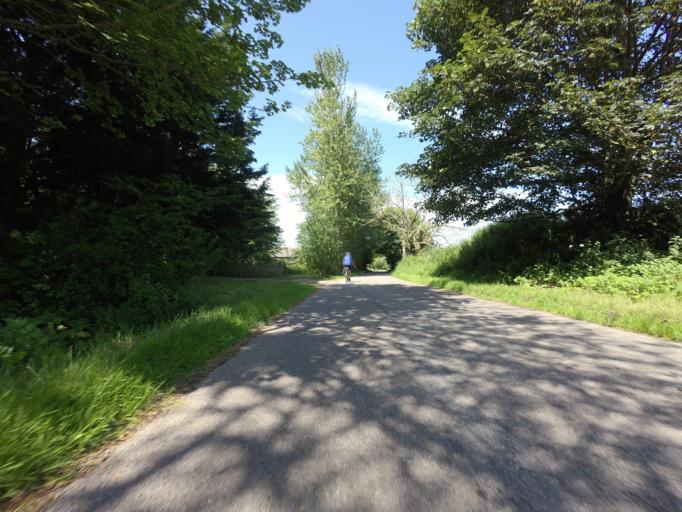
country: GB
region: Scotland
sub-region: Highland
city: Conon Bridge
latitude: 57.5543
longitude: -4.4075
